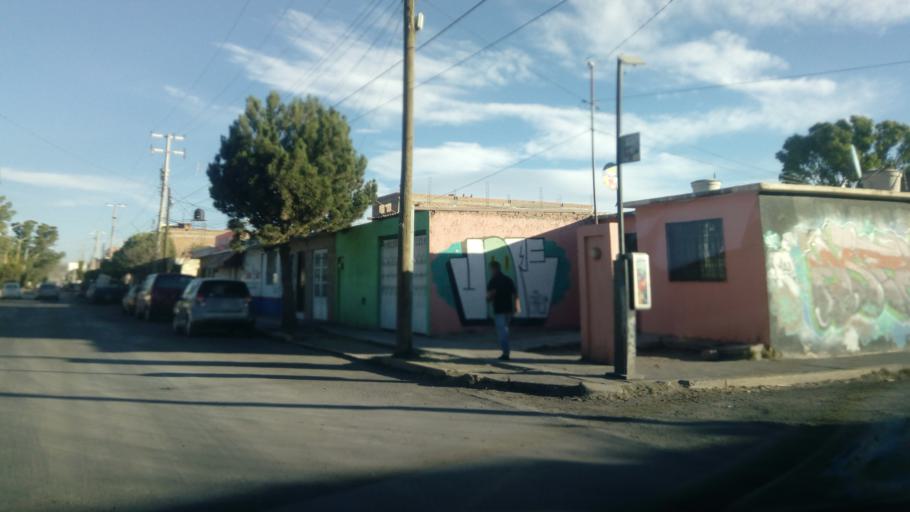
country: MX
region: Durango
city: Victoria de Durango
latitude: 24.0627
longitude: -104.5961
